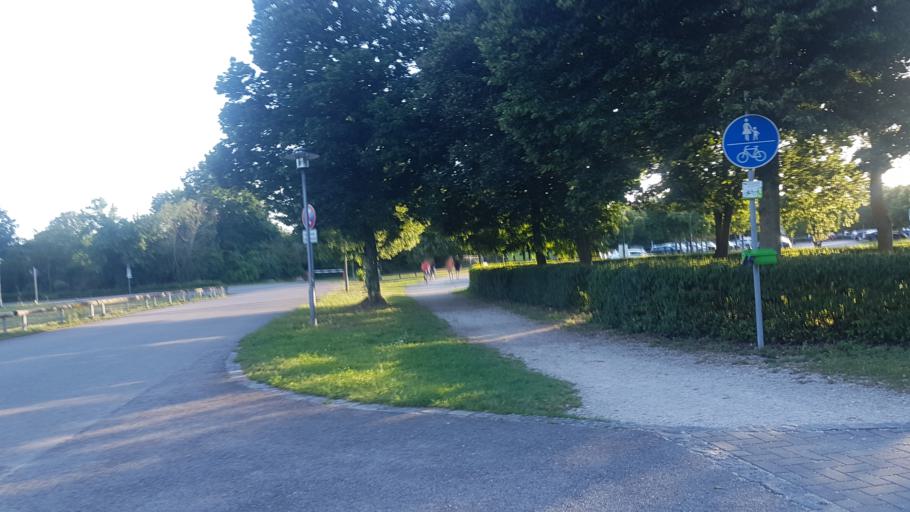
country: DE
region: Bavaria
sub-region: Regierungsbezirk Mittelfranken
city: Gunzenhausen
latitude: 49.1263
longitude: 10.7416
